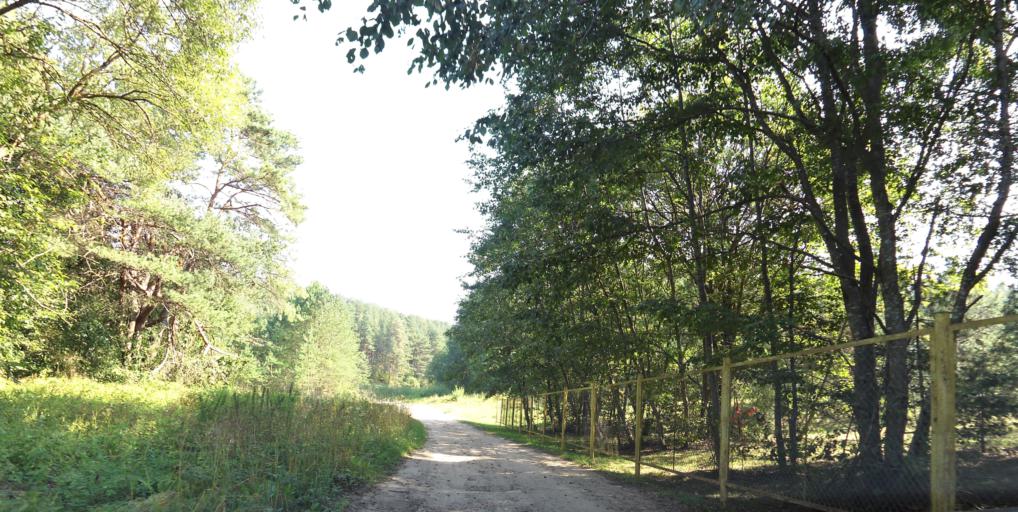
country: LT
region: Vilnius County
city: Pilaite
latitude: 54.6984
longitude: 25.1941
